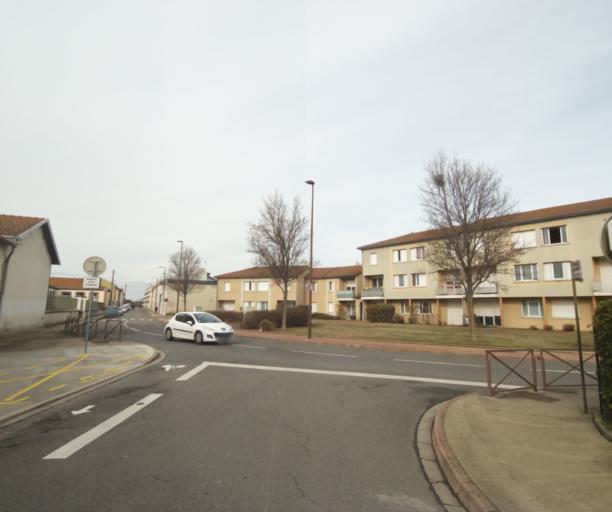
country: FR
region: Rhone-Alpes
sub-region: Departement de la Loire
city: Roanne
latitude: 46.0294
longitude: 4.0643
